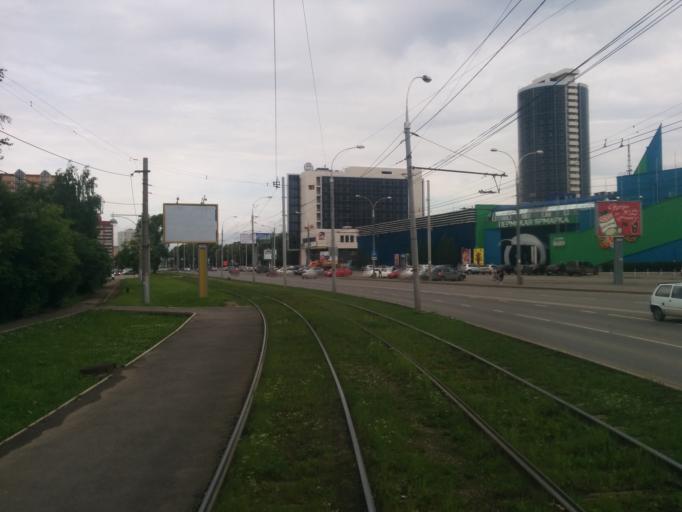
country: RU
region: Perm
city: Perm
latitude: 58.0041
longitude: 56.2861
